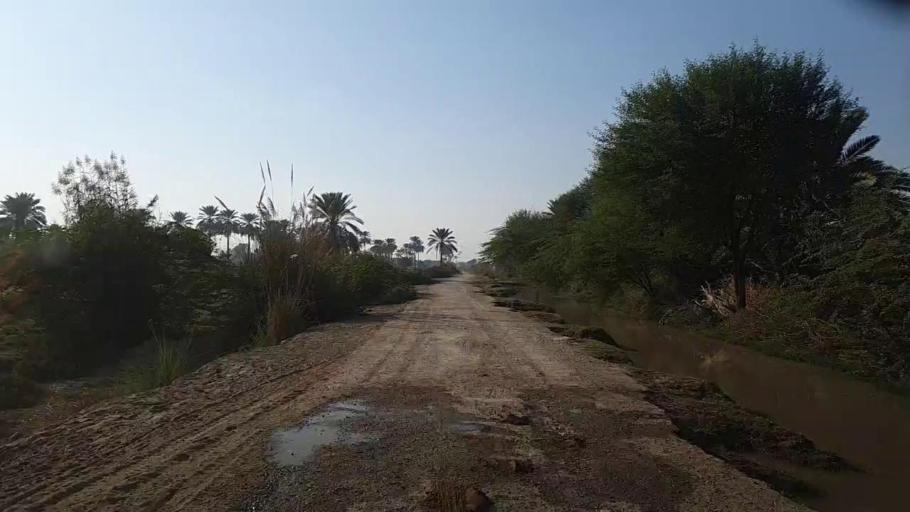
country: PK
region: Sindh
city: Ranipur
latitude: 27.2529
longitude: 68.5411
